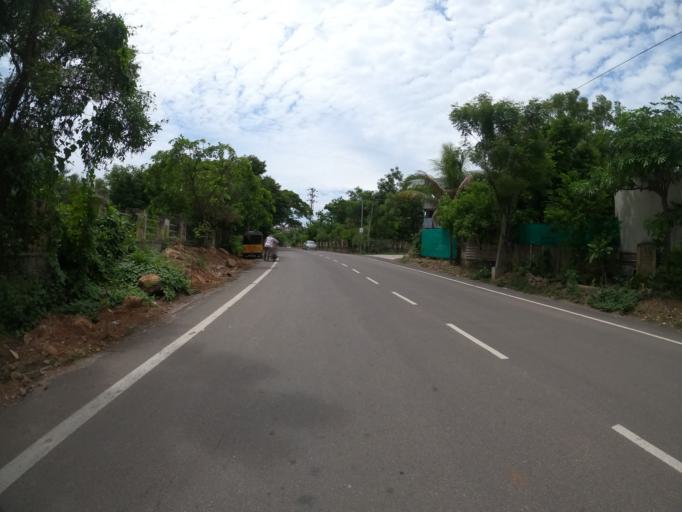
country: IN
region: Telangana
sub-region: Hyderabad
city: Hyderabad
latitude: 17.3664
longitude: 78.4151
